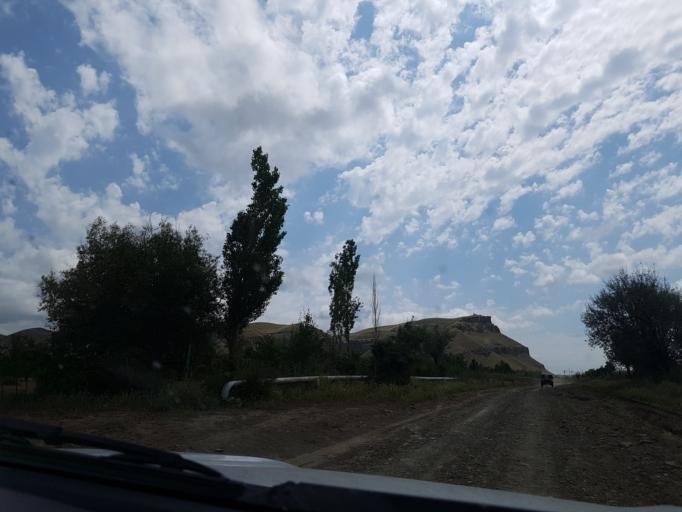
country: TM
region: Ahal
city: Baharly
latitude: 38.2232
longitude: 56.8934
